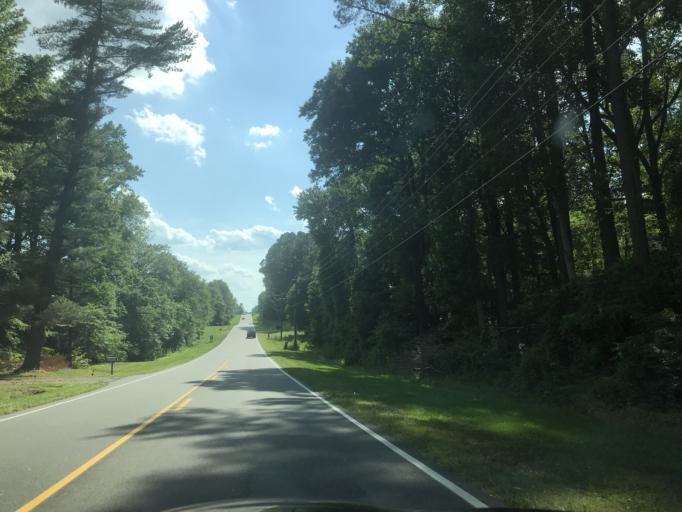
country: US
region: North Carolina
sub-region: Nash County
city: Spring Hope
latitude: 35.9573
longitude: -78.0764
